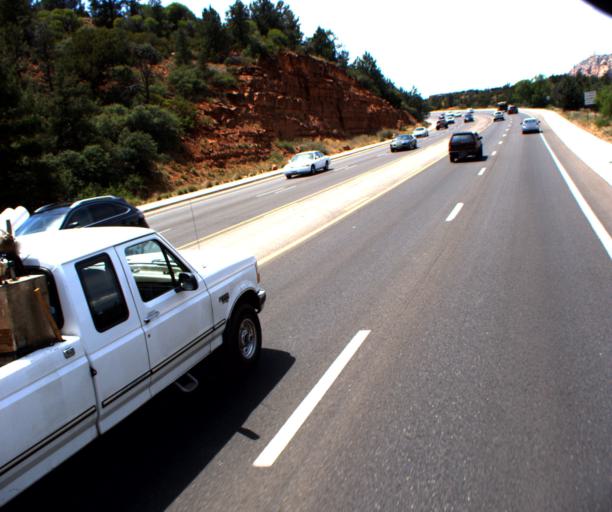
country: US
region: Arizona
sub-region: Coconino County
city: Sedona
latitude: 34.8671
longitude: -111.7684
